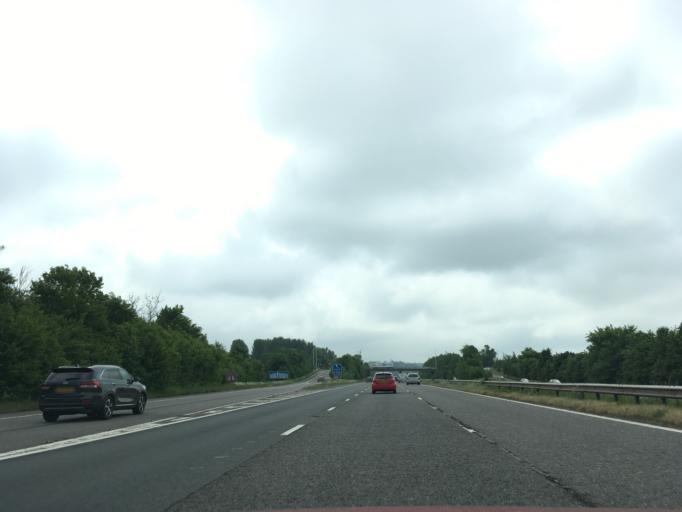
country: GB
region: England
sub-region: Devon
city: Cullompton
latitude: 50.8643
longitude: -3.3832
